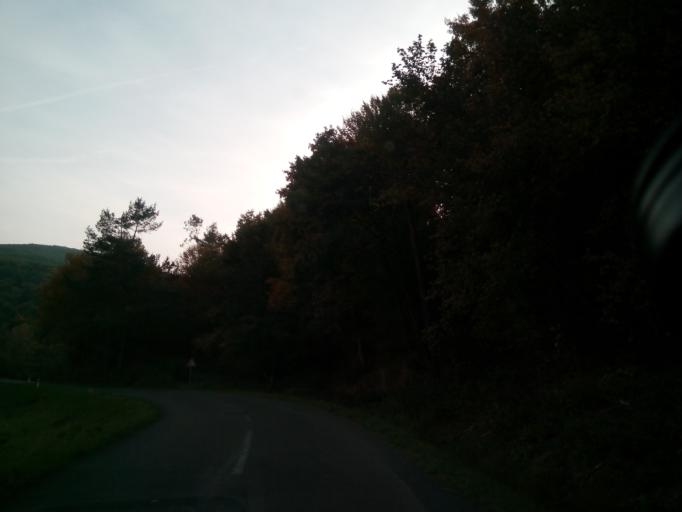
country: SK
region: Presovsky
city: Svidnik
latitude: 49.3539
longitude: 21.4652
